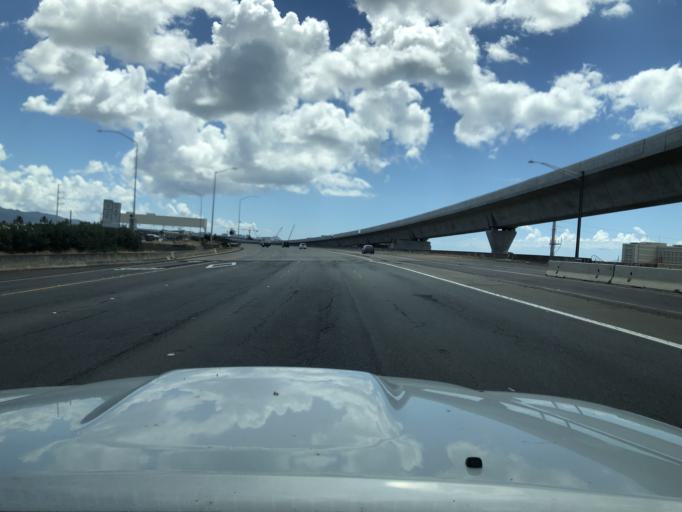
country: US
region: Hawaii
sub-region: Honolulu County
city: Hickam Field
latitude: 21.3409
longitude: -157.9307
